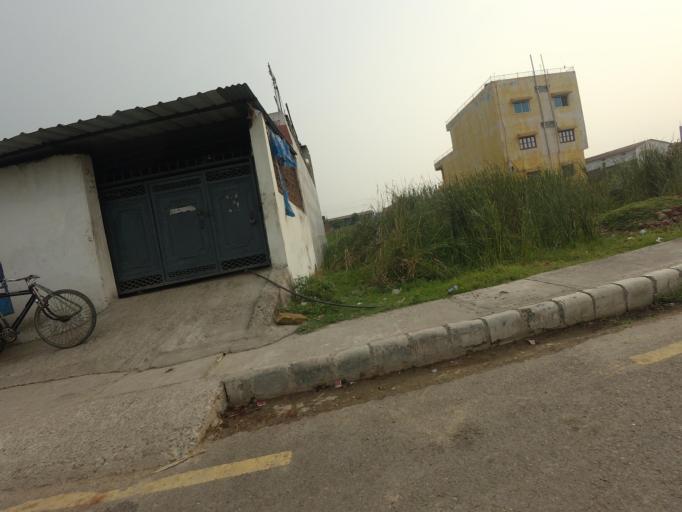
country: NP
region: Western Region
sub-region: Lumbini Zone
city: Bhairahawa
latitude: 27.5051
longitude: 83.4439
